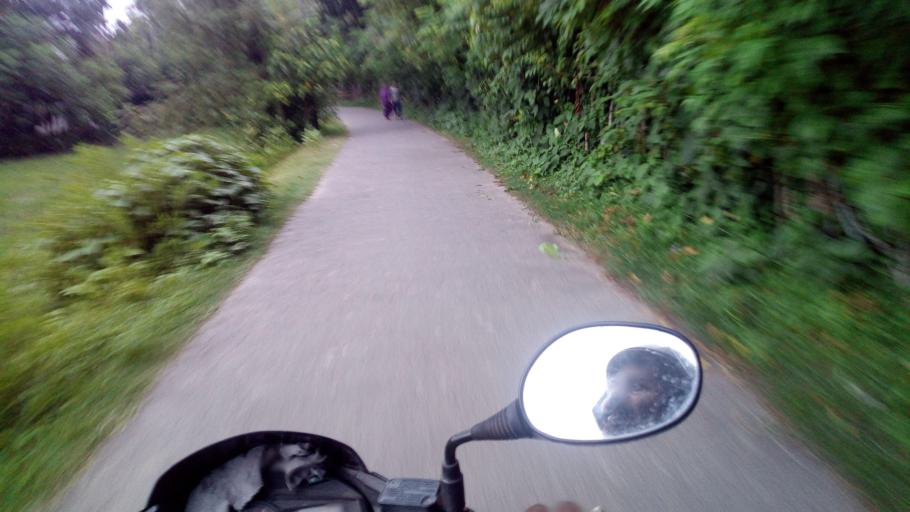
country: BD
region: Khulna
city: Phultala
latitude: 22.7545
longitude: 89.4073
